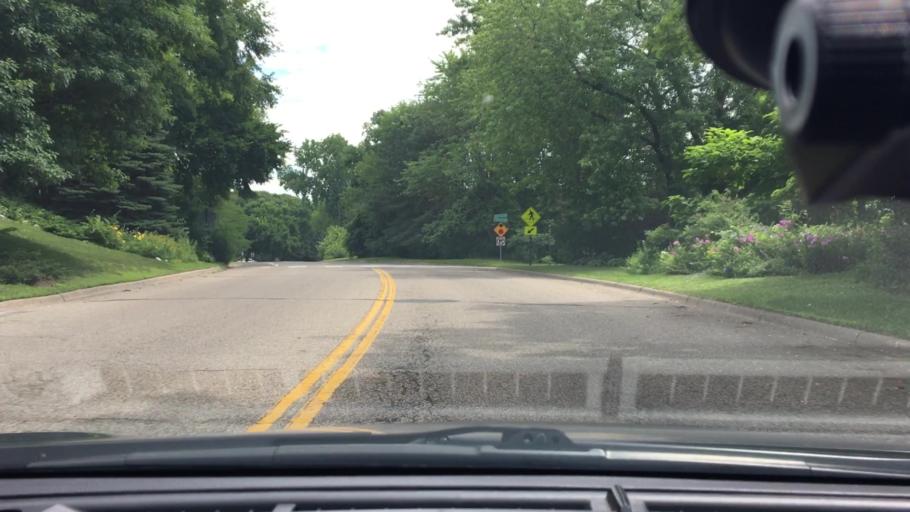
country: US
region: Minnesota
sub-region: Hennepin County
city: New Hope
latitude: 45.0128
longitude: -93.4152
